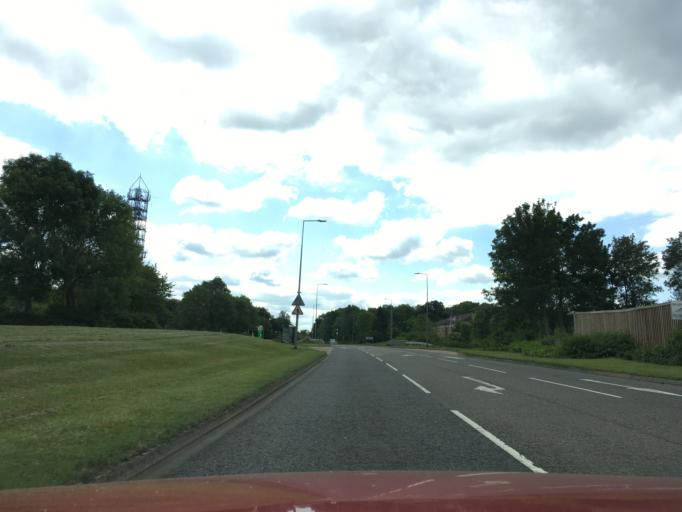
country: GB
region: England
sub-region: Milton Keynes
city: Bradwell
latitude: 52.0546
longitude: -0.7711
